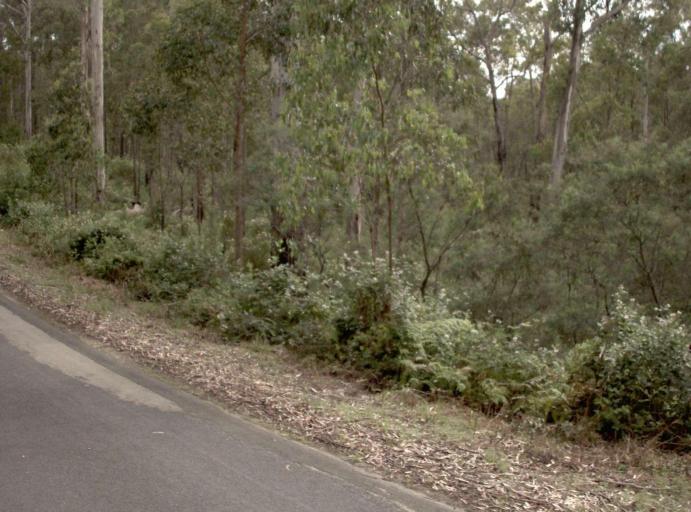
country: AU
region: Victoria
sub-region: East Gippsland
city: Bairnsdale
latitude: -37.7099
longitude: 147.5928
